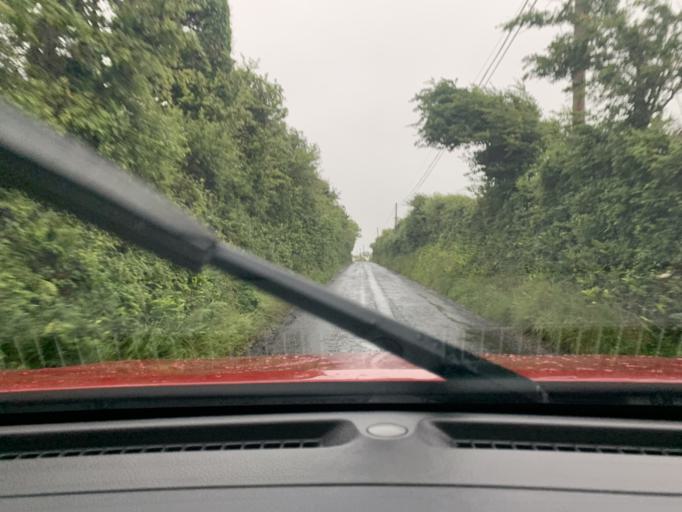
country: IE
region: Connaught
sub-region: County Leitrim
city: Kinlough
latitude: 54.4434
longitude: -8.4406
